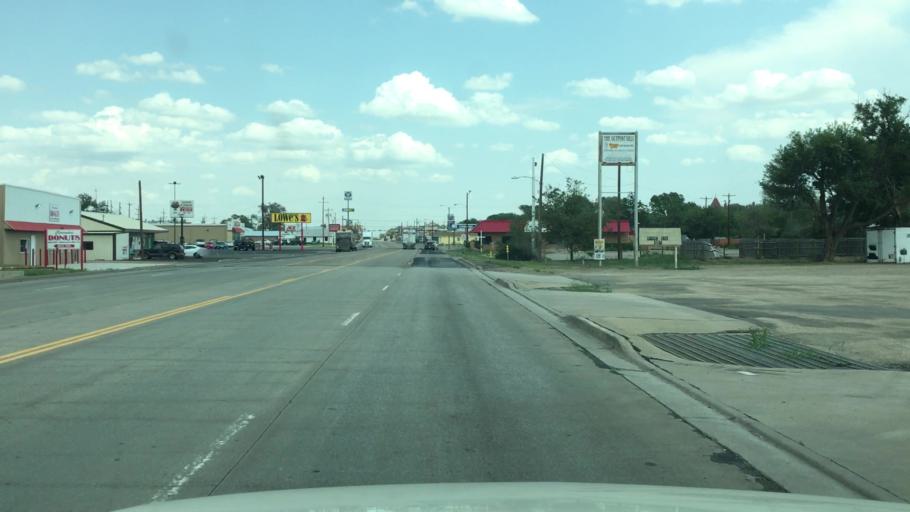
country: US
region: Texas
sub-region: Donley County
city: Clarendon
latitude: 34.9408
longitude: -100.8941
